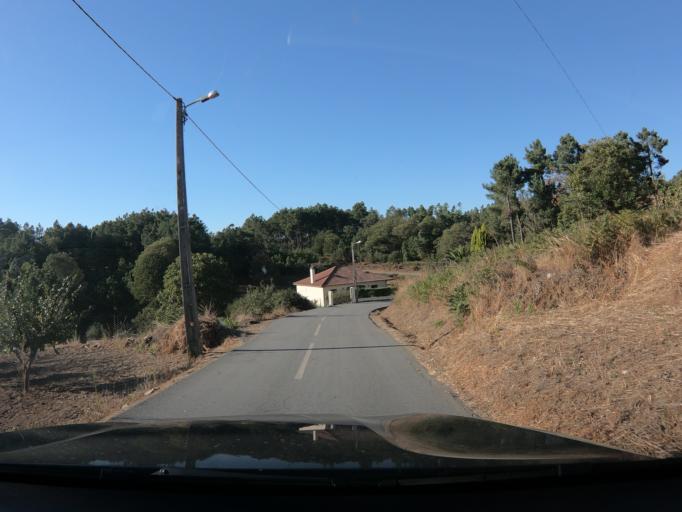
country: PT
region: Vila Real
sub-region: Sabrosa
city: Vilela
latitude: 41.2416
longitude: -7.6184
